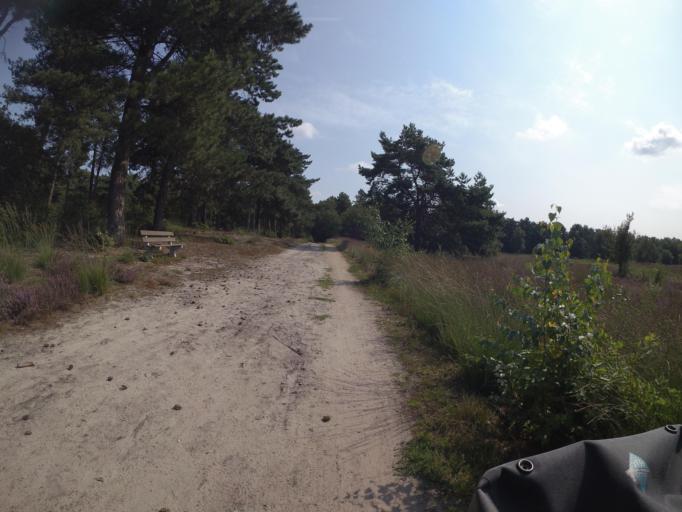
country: NL
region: Limburg
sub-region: Gemeente Venray
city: Venray
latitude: 51.4689
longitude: 5.9043
